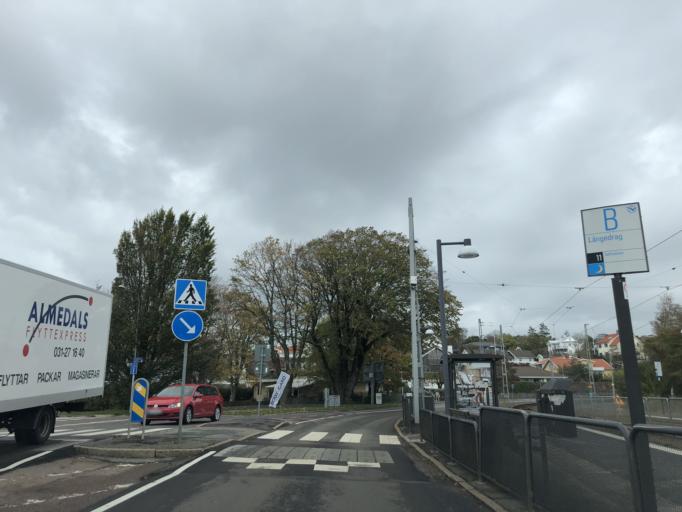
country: SE
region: Vaestra Goetaland
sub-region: Goteborg
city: Majorna
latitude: 57.6678
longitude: 11.8534
